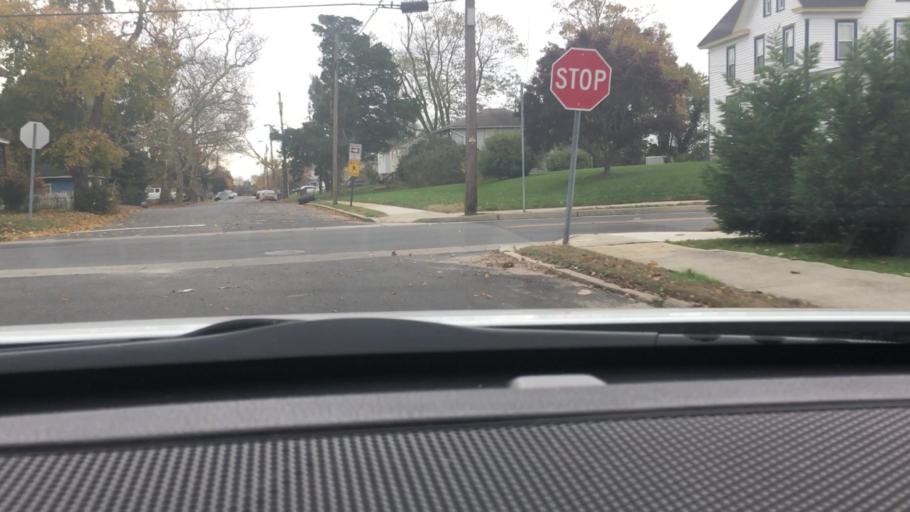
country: US
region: New Jersey
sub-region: Atlantic County
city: Northfield
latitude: 39.3780
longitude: -74.5362
